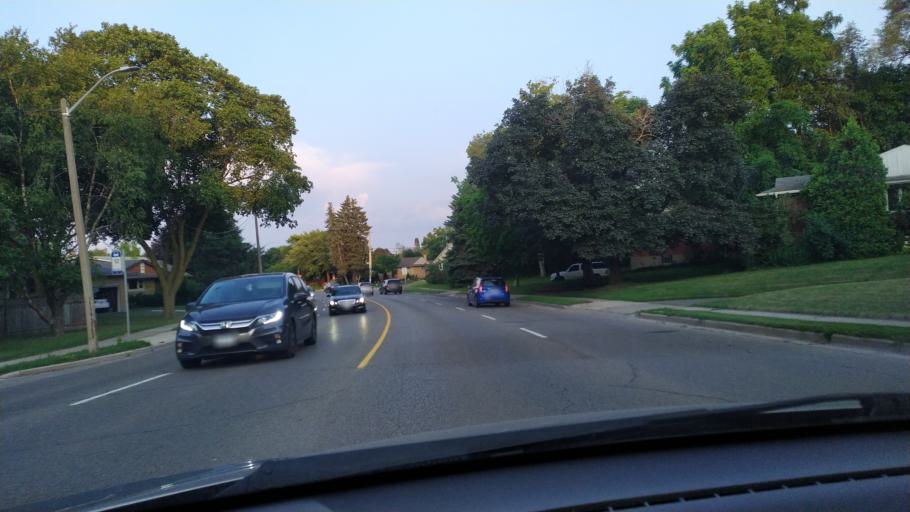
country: CA
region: Ontario
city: Waterloo
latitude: 43.4575
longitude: -80.5351
